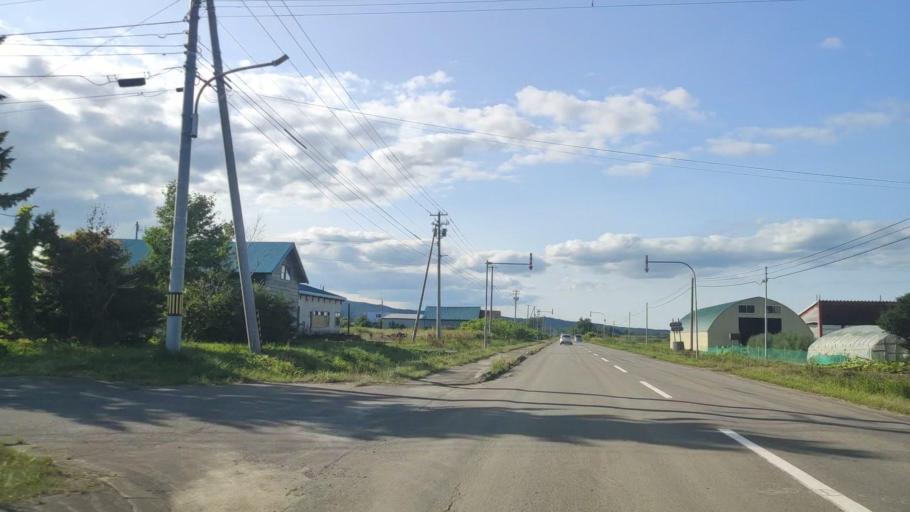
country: JP
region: Hokkaido
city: Makubetsu
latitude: 44.8241
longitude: 142.0646
